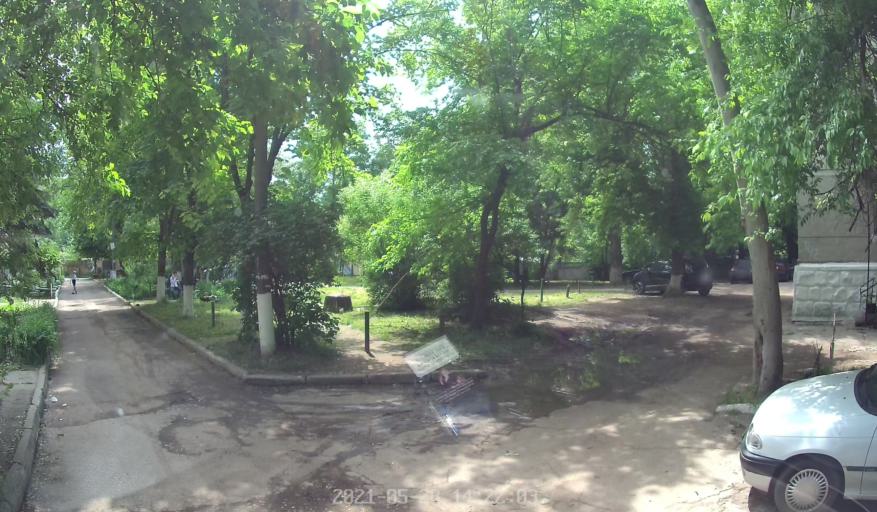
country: MD
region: Chisinau
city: Chisinau
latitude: 47.0461
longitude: 28.8567
